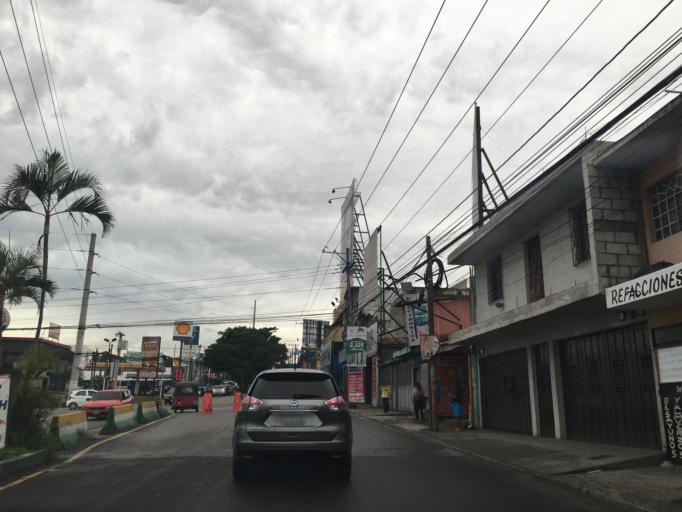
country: GT
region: Guatemala
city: Petapa
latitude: 14.5243
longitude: -90.5516
